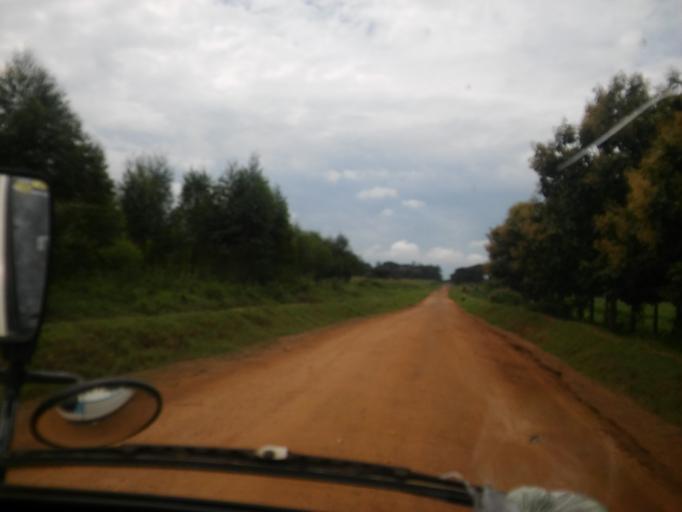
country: UG
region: Eastern Region
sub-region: Bududa District
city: Bududa
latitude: 0.9455
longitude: 34.2349
